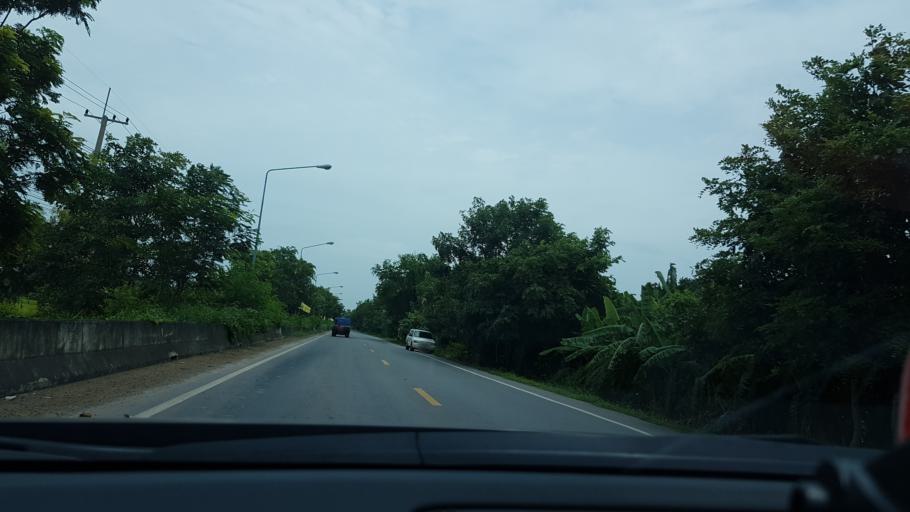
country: TH
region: Pathum Thani
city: Sam Khok
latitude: 14.1257
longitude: 100.5452
